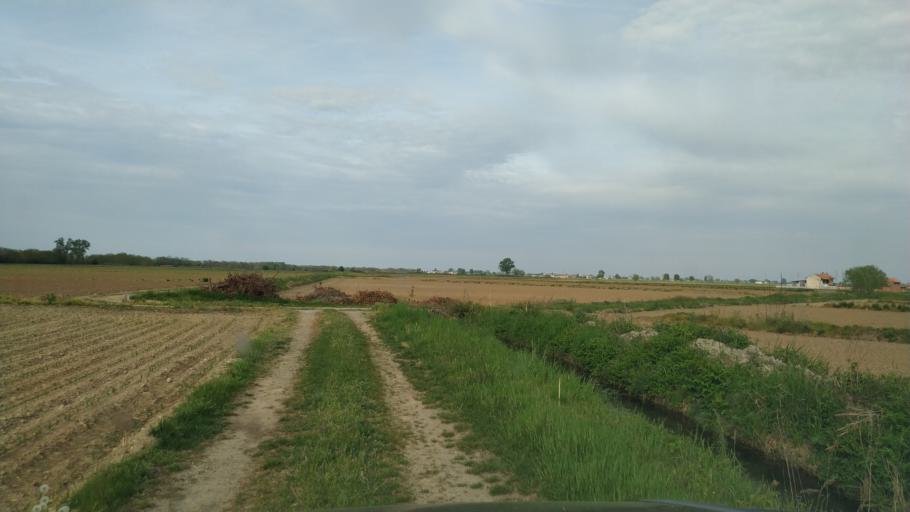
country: IT
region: Piedmont
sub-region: Provincia di Vercelli
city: Bianze
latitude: 45.3456
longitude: 8.1235
